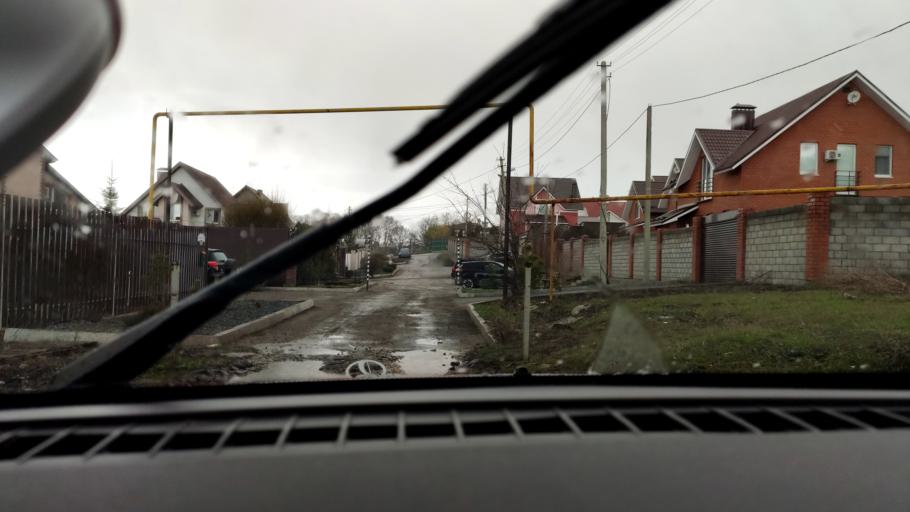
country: RU
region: Samara
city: Novosemeykino
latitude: 53.3302
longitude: 50.2887
